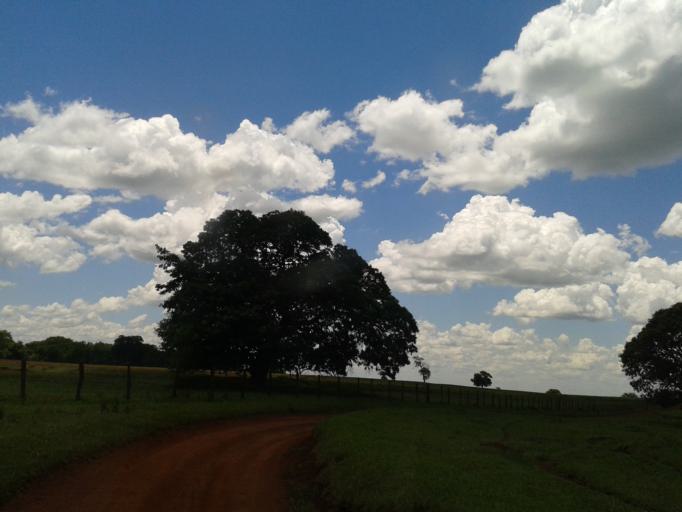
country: BR
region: Minas Gerais
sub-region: Centralina
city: Centralina
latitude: -18.6974
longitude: -49.1863
